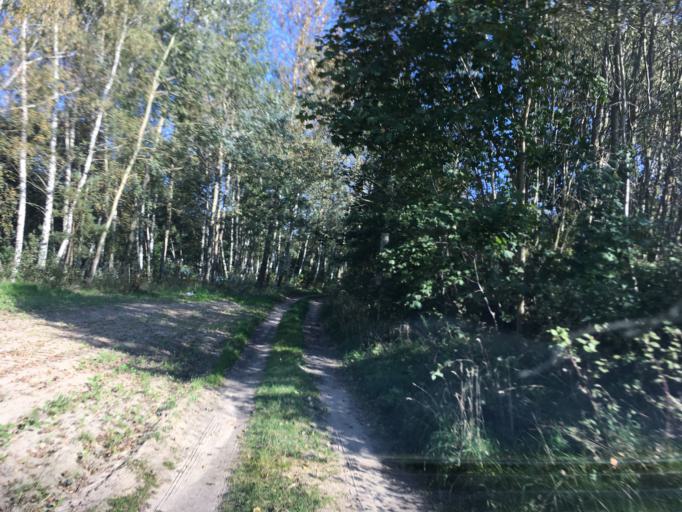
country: PL
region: Kujawsko-Pomorskie
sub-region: Powiat brodnicki
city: Bartniczka
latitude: 53.2843
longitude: 19.6883
